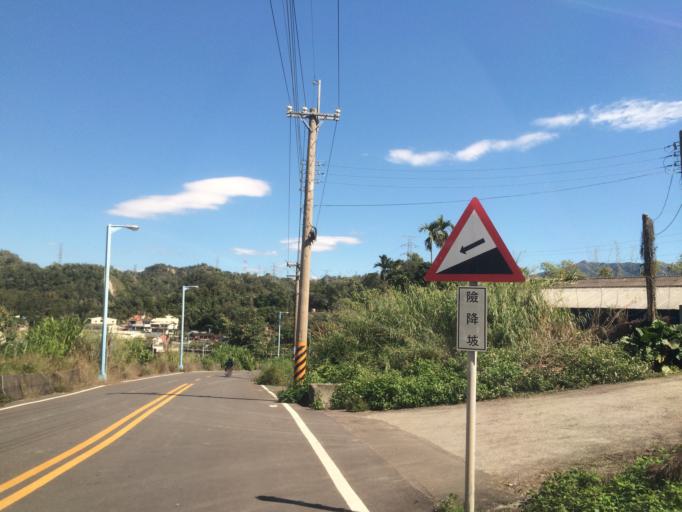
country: TW
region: Taiwan
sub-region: Yunlin
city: Douliu
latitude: 23.6910
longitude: 120.6202
